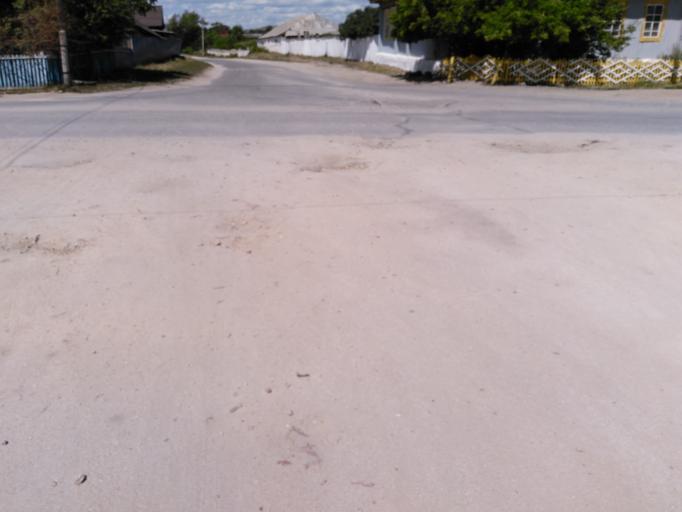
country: RU
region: Bashkortostan
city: Akhunovo
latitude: 54.2094
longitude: 59.6060
